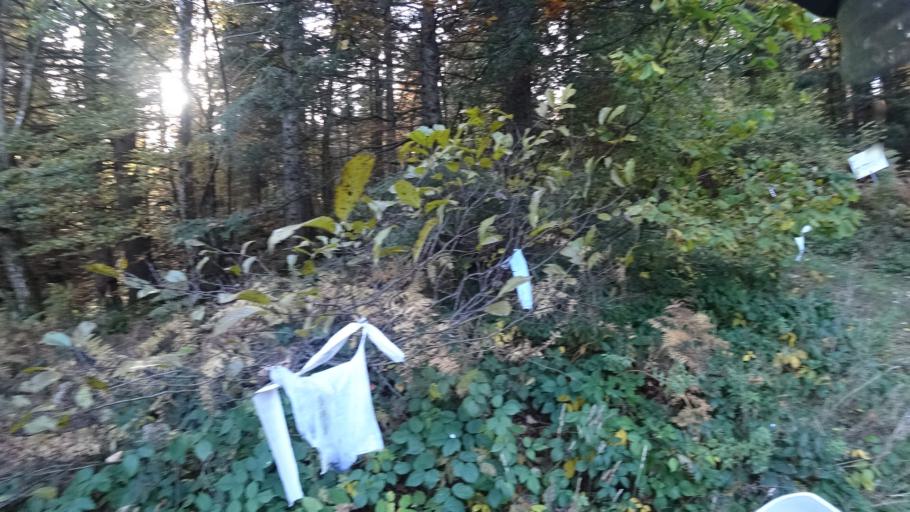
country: HR
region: Karlovacka
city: Plaski
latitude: 44.9828
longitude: 15.4032
